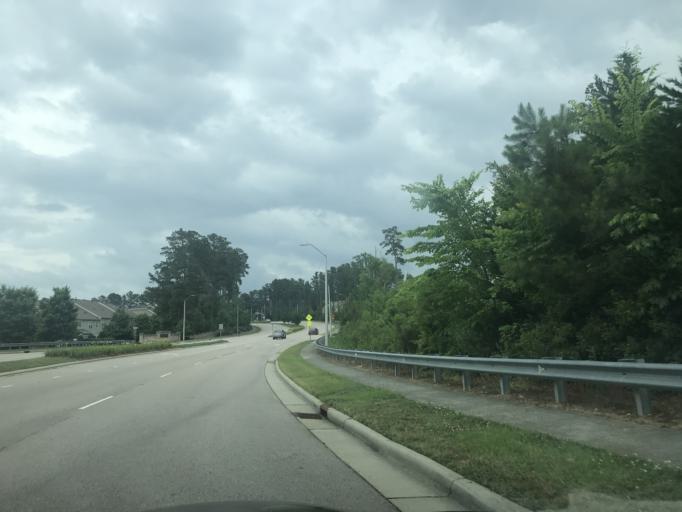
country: US
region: North Carolina
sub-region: Wake County
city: Morrisville
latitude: 35.8148
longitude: -78.8517
